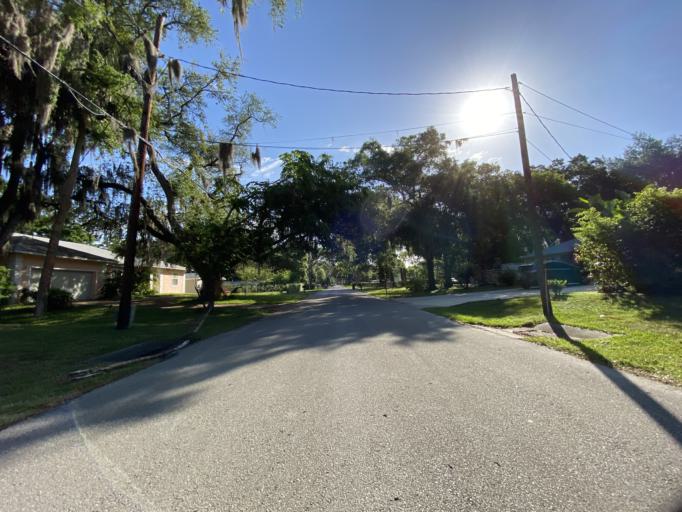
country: US
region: Florida
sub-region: Volusia County
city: South Daytona
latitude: 29.1764
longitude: -81.0207
